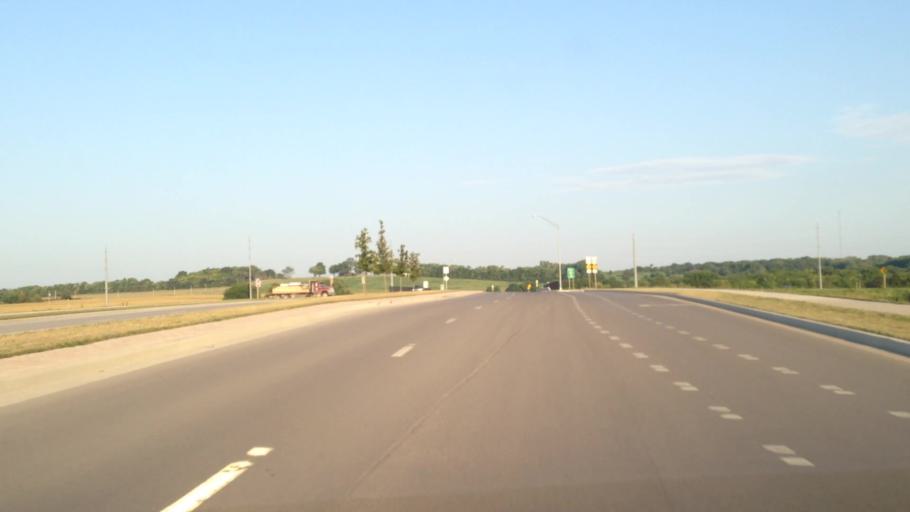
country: US
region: Kansas
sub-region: Douglas County
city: Lawrence
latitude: 38.9570
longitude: -95.3525
